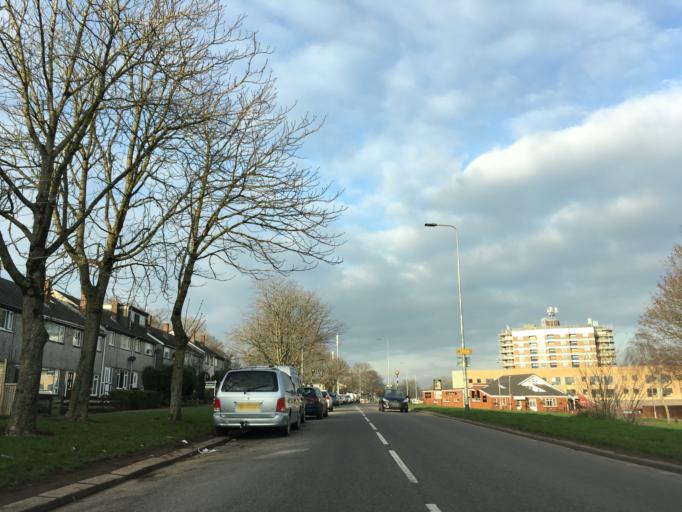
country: GB
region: Wales
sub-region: Cardiff
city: Cardiff
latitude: 51.5111
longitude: -3.1536
